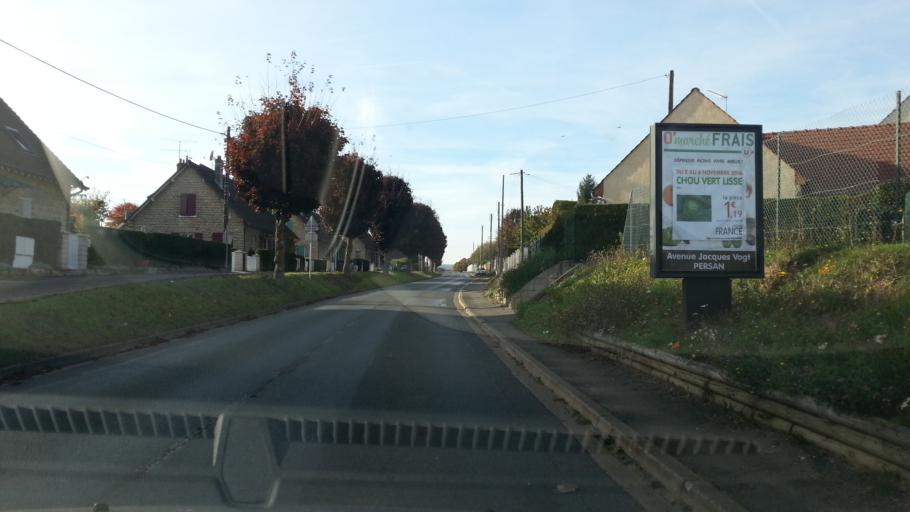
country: FR
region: Picardie
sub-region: Departement de l'Oise
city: Chambly
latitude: 49.1668
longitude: 2.2612
